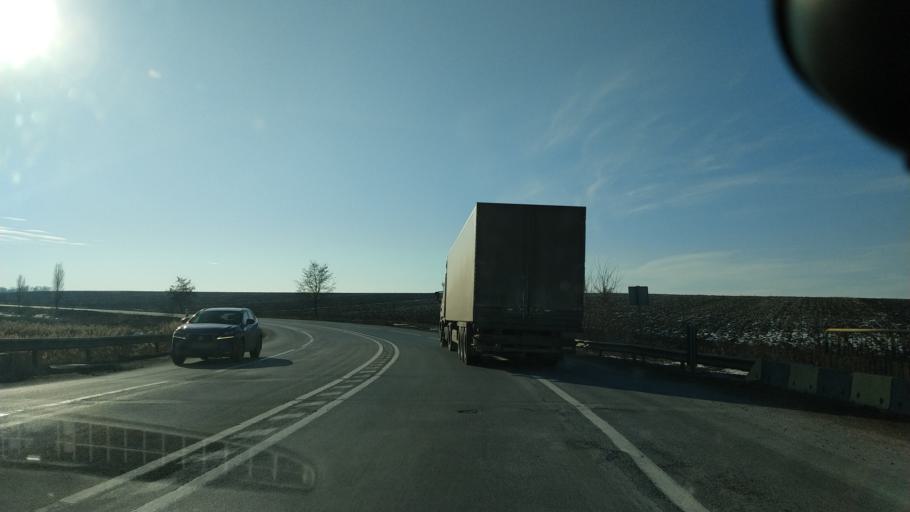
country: RO
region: Iasi
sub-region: Comuna Butea
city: Butea
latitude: 47.1106
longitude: 26.9268
